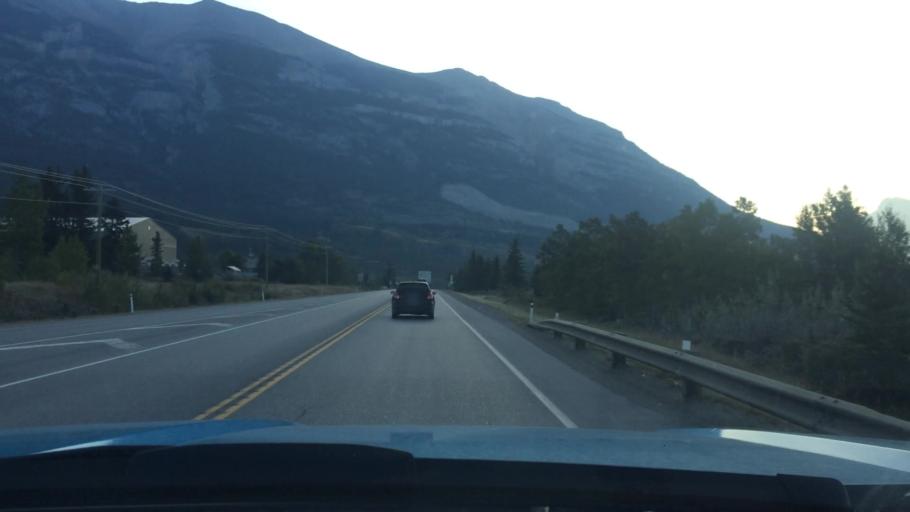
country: CA
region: Alberta
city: Canmore
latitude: 51.0750
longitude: -115.3266
